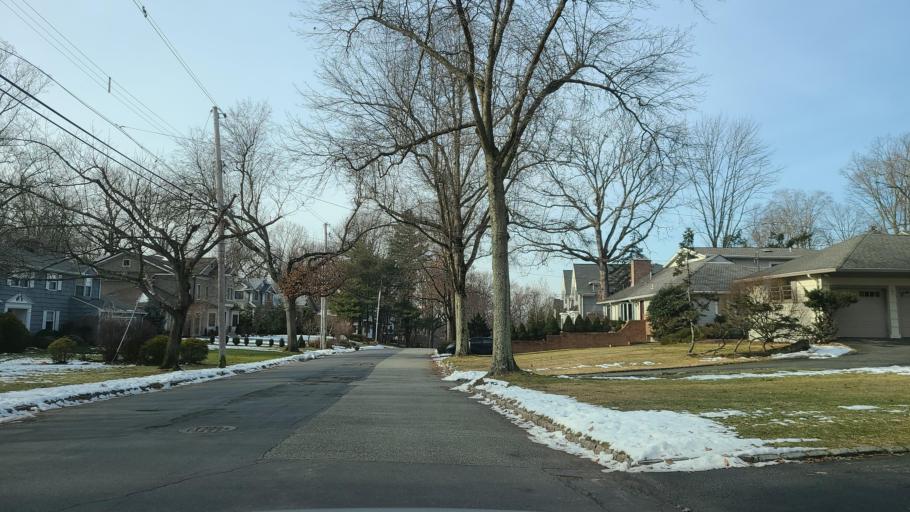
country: US
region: New Jersey
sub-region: Union County
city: Summit
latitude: 40.7328
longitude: -74.3450
